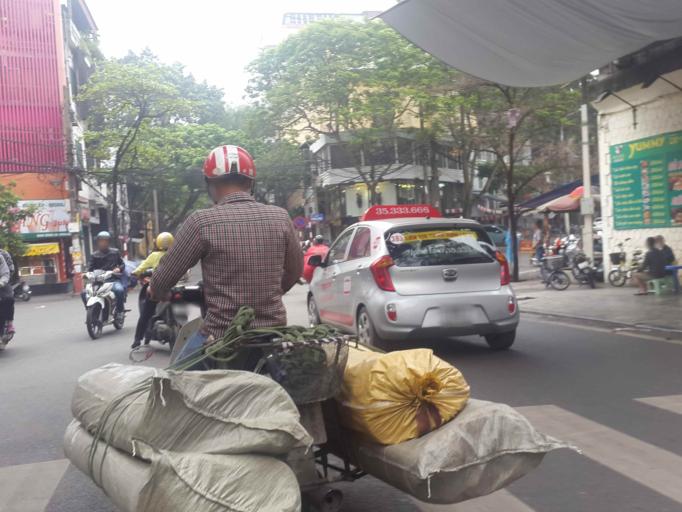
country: VN
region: Ha Noi
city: Hoan Kiem
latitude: 21.0389
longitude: 105.8471
